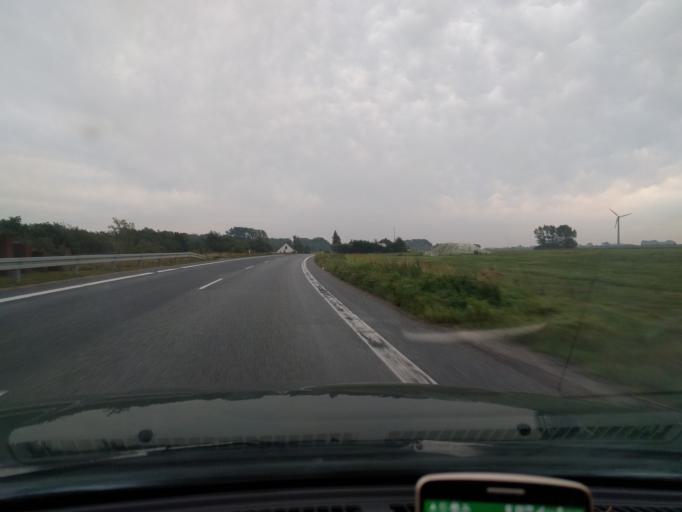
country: DK
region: Zealand
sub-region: Guldborgsund Kommune
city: Norre Alslev
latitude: 54.9332
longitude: 11.8701
